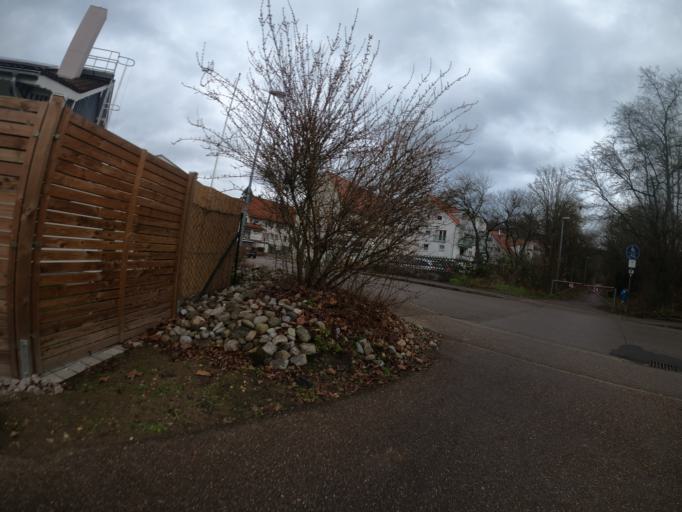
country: DE
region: Baden-Wuerttemberg
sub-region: Regierungsbezirk Stuttgart
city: Donzdorf
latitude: 48.6838
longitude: 9.8067
